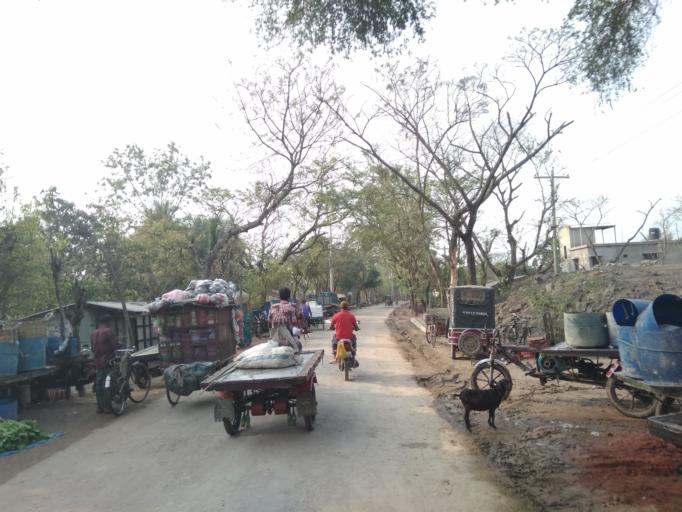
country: IN
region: West Bengal
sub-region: North 24 Parganas
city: Taki
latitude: 22.3173
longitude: 89.1062
